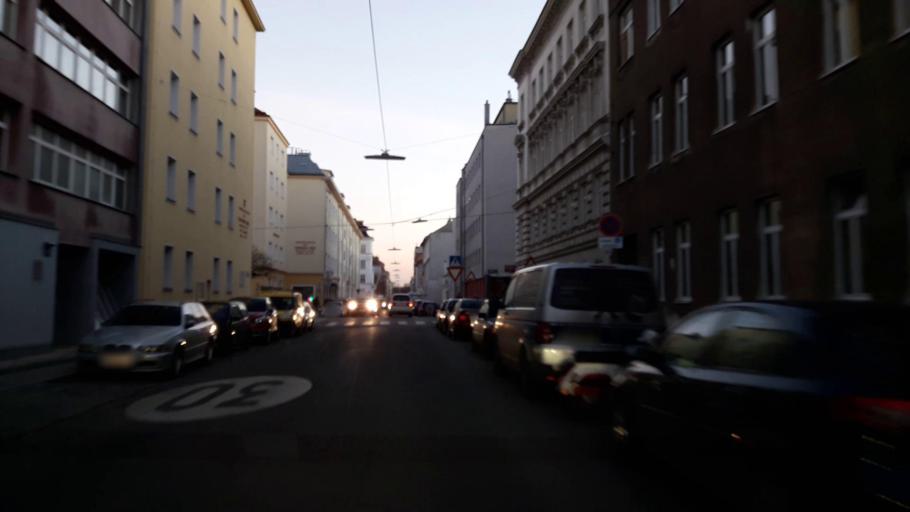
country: AT
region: Vienna
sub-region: Wien Stadt
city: Vienna
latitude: 48.1821
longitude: 16.4086
